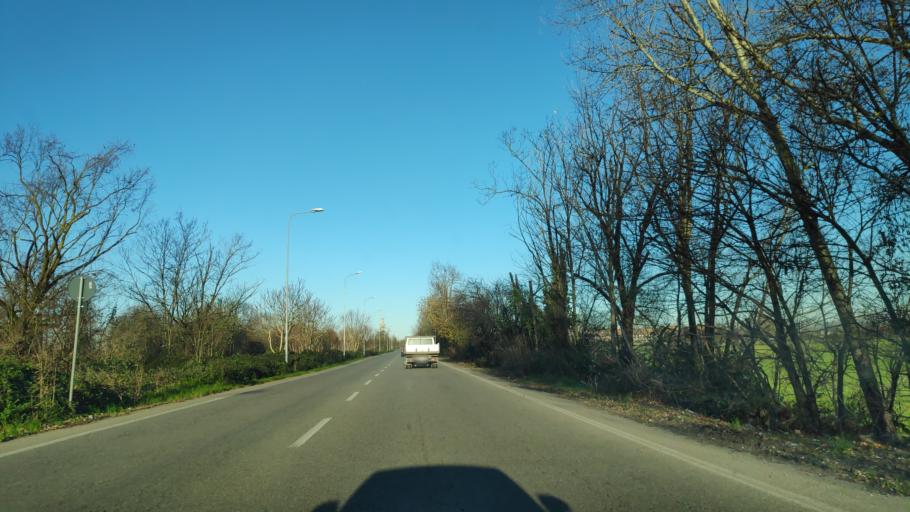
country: IT
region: Lombardy
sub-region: Citta metropolitana di Milano
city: Fizzonasco
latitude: 45.3608
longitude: 9.1948
